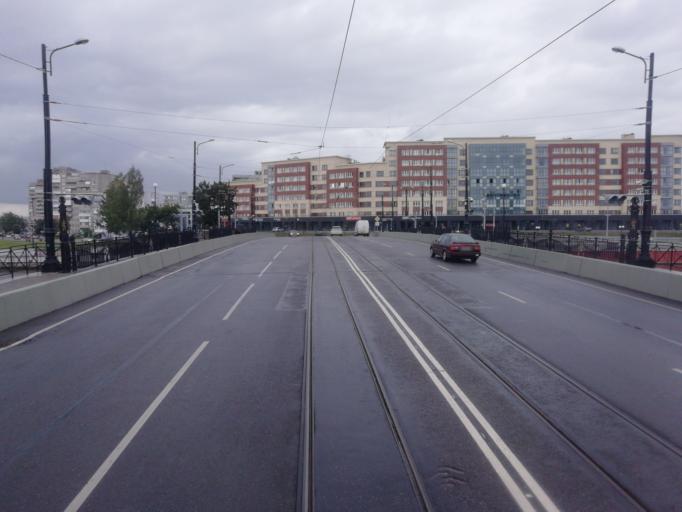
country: RU
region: Kaliningrad
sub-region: Gorod Kaliningrad
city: Kaliningrad
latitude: 54.6989
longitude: 20.5174
